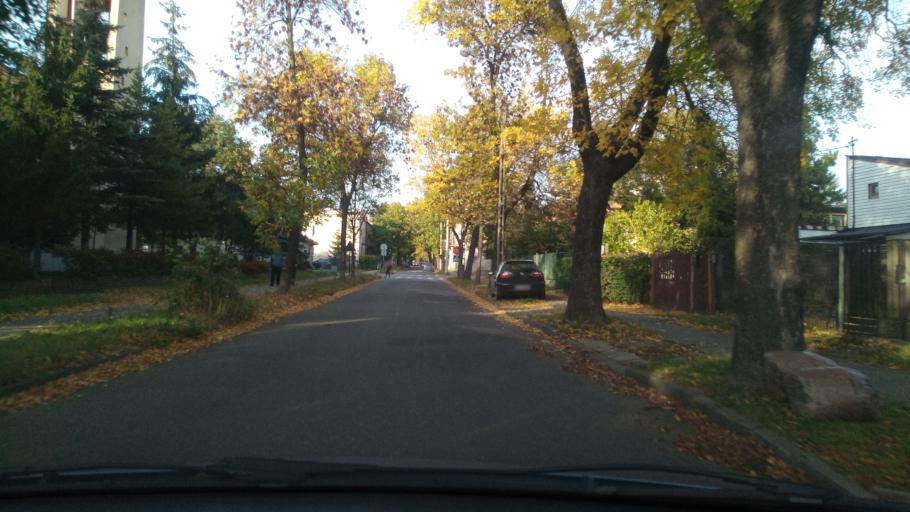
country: PL
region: Silesian Voivodeship
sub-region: Sosnowiec
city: Sosnowiec
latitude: 50.2816
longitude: 19.1121
